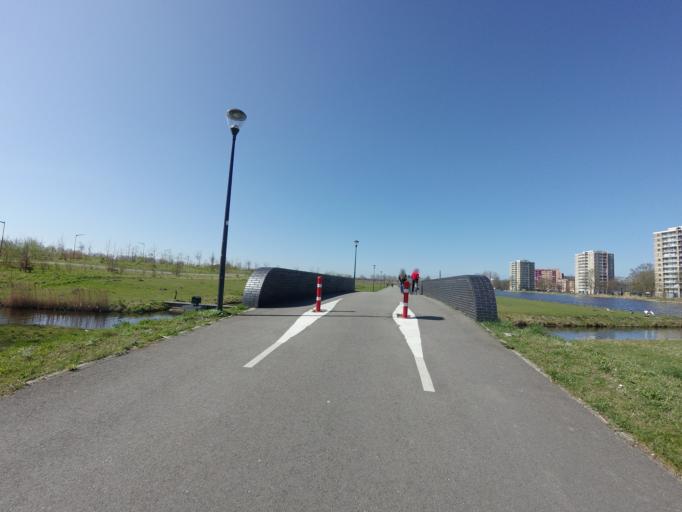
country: NL
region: North Holland
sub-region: Gemeente Haarlem
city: Haarlem
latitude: 52.3722
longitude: 4.6654
